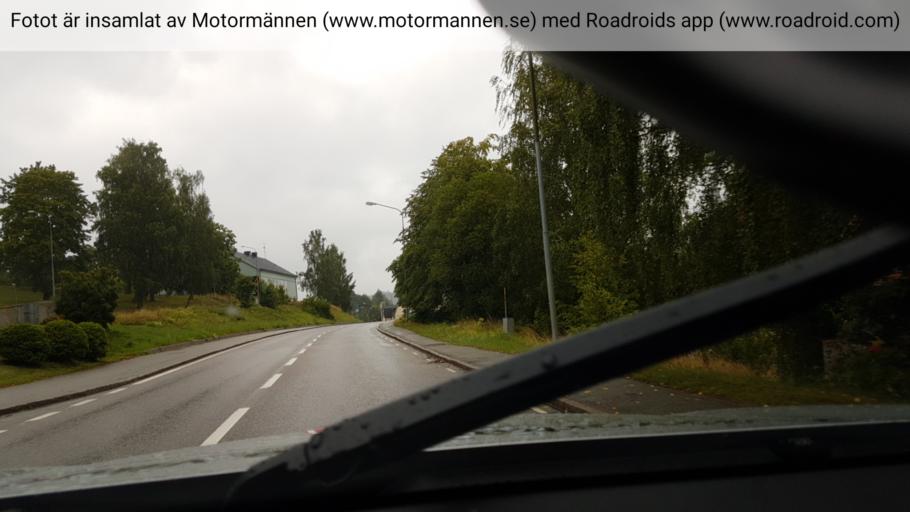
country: SE
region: Vaestra Goetaland
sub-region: Bengtsfors Kommun
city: Billingsfors
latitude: 58.9811
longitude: 12.2485
